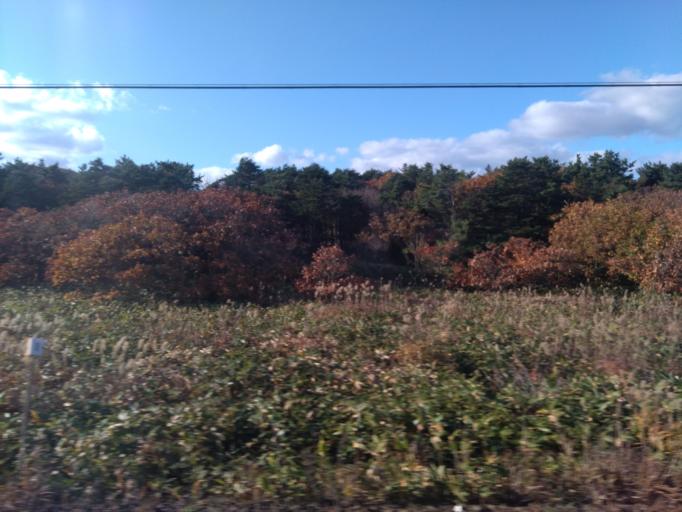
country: JP
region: Hokkaido
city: Niseko Town
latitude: 42.5548
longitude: 140.4228
